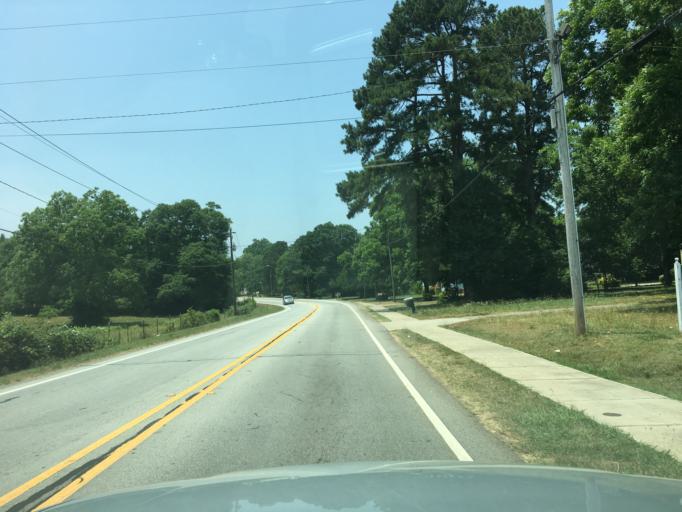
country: US
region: Georgia
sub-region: Hart County
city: Royston
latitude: 34.2883
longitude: -83.0990
